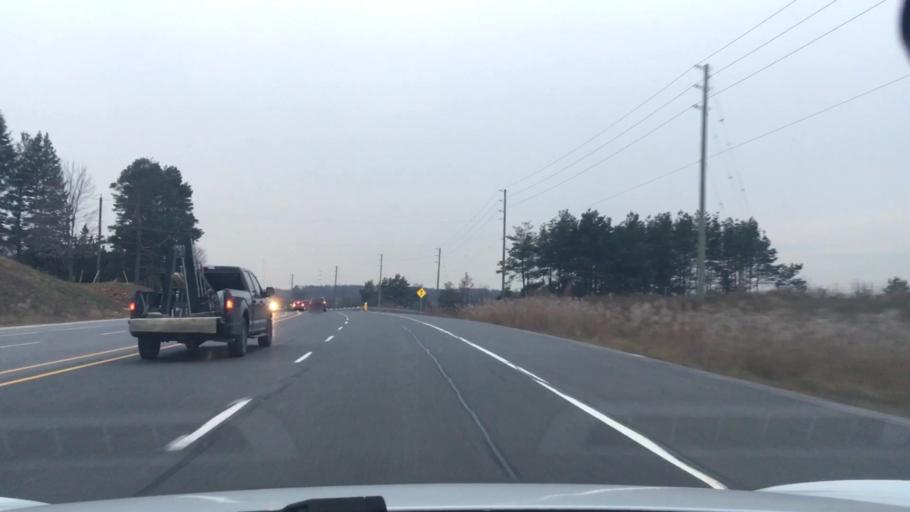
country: CA
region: Ontario
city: Pickering
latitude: 43.9345
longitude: -79.0640
